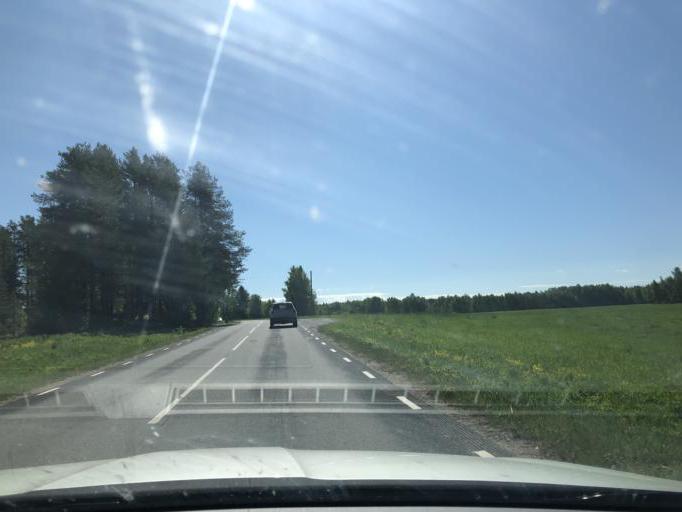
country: SE
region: Norrbotten
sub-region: Lulea Kommun
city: Gammelstad
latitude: 65.6586
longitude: 21.9947
